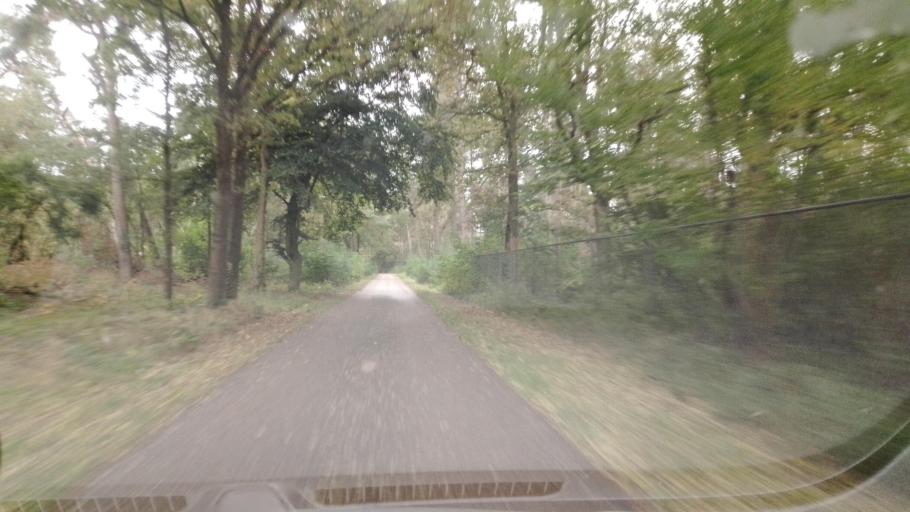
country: NL
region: Limburg
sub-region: Gemeente Venlo
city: Venlo
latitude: 51.4007
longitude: 6.1249
